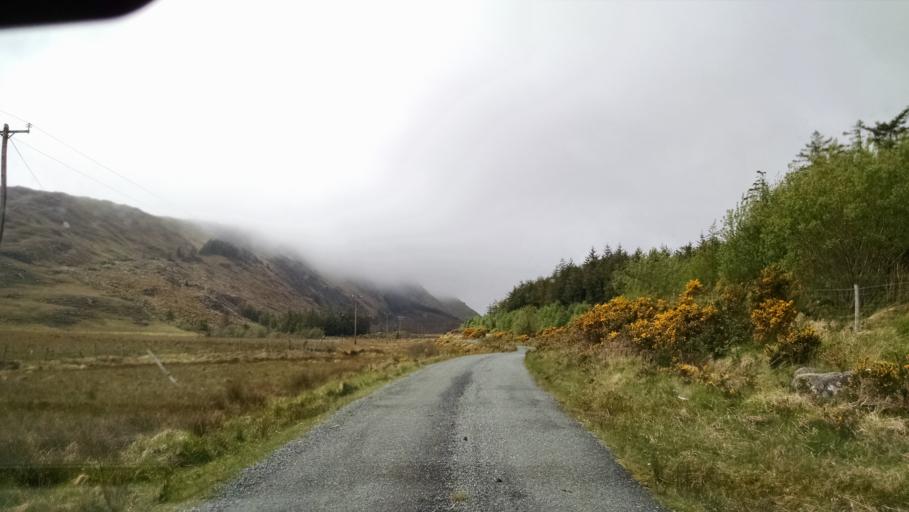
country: IE
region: Connaught
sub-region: Maigh Eo
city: Westport
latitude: 53.6445
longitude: -9.6731
